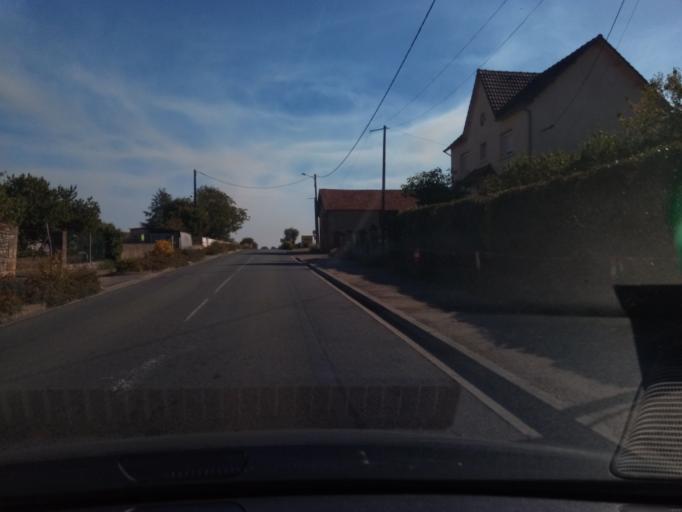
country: FR
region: Poitou-Charentes
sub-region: Departement de la Vienne
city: Saint-Savin
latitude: 46.5047
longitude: 0.7763
